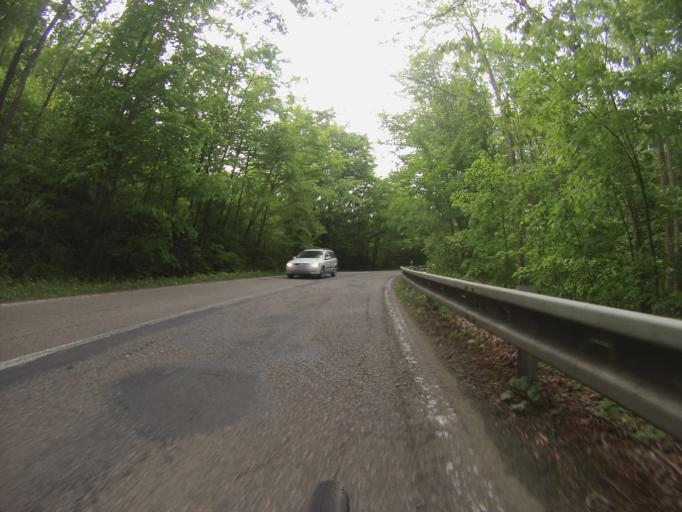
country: CZ
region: South Moravian
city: Veverska Bityska
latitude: 49.2528
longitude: 16.4796
